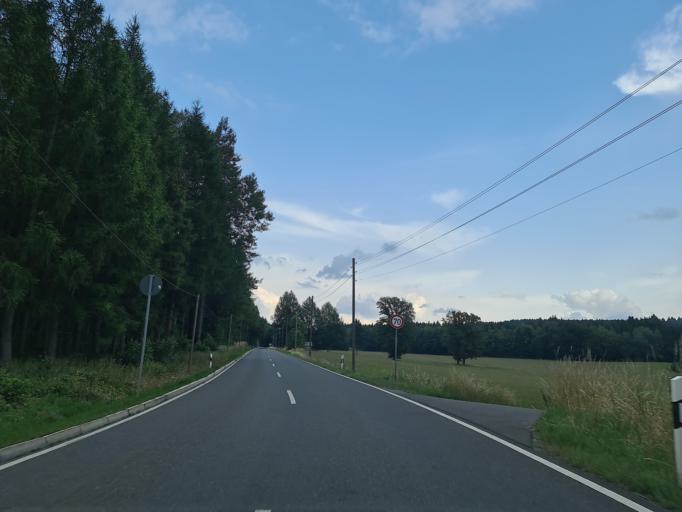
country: DE
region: Saxony
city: Bergen
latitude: 50.4634
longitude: 12.2883
